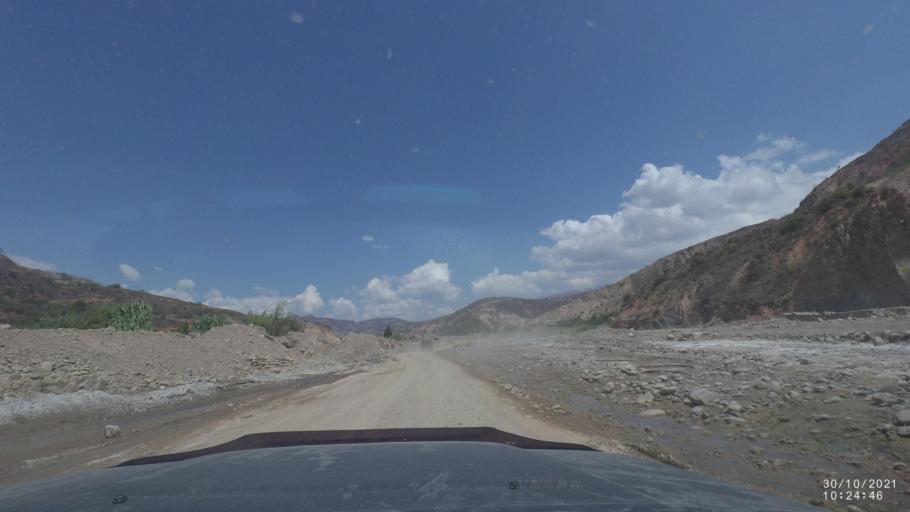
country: BO
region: Cochabamba
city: Sipe Sipe
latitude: -17.5527
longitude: -66.3908
